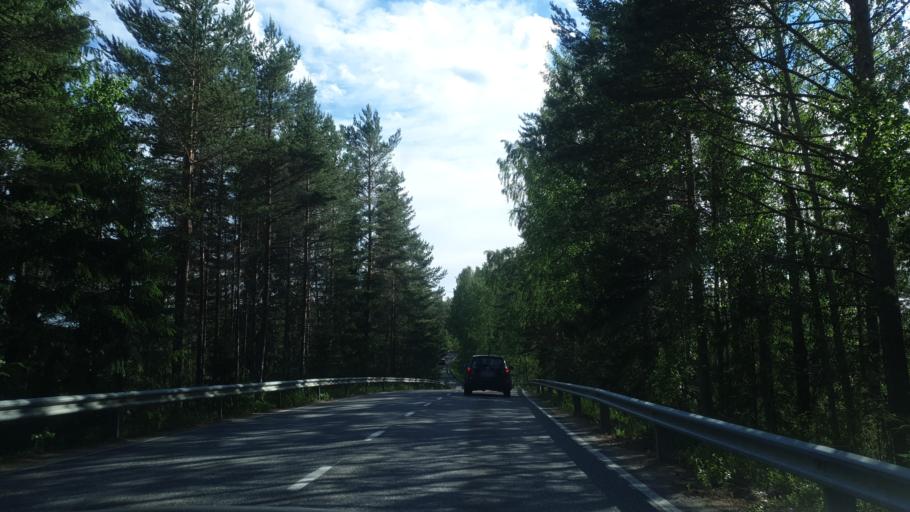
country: FI
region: Southern Savonia
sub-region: Mikkeli
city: Pertunmaa
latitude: 61.4925
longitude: 26.4763
